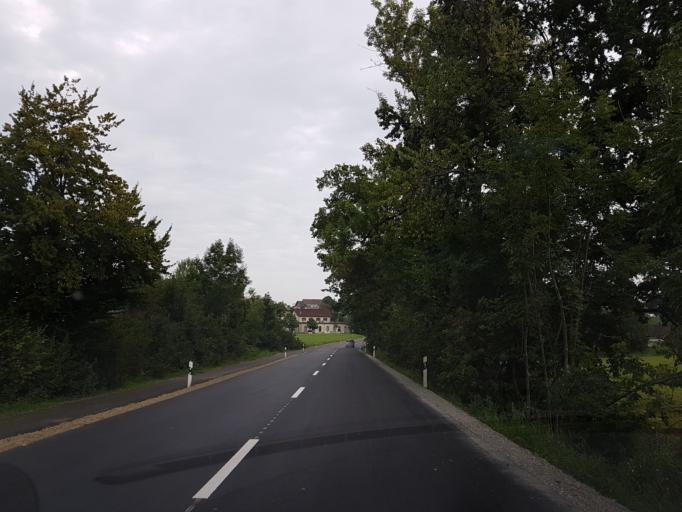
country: CH
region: Zurich
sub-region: Bezirk Affoltern
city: Obfelden / Oberlunnern
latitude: 47.2648
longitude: 8.4036
